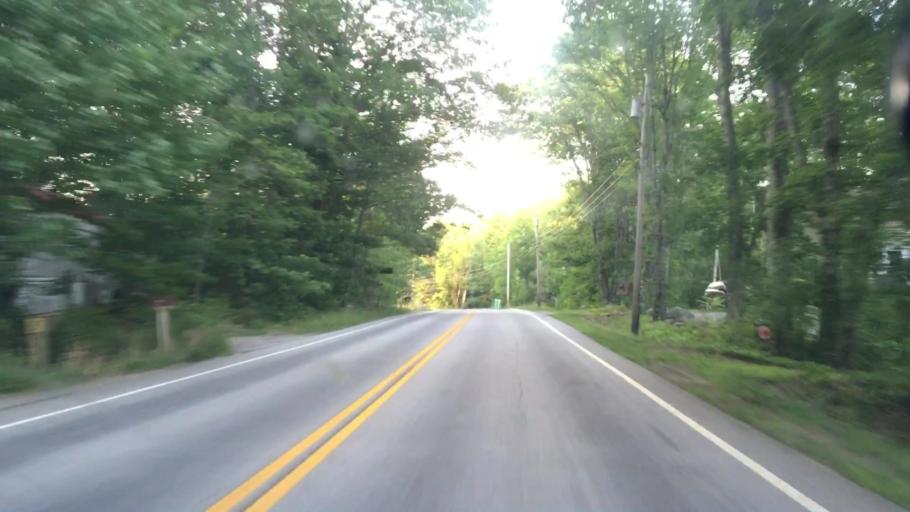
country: US
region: Maine
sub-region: Waldo County
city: Frankfort
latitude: 44.6773
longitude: -68.9194
